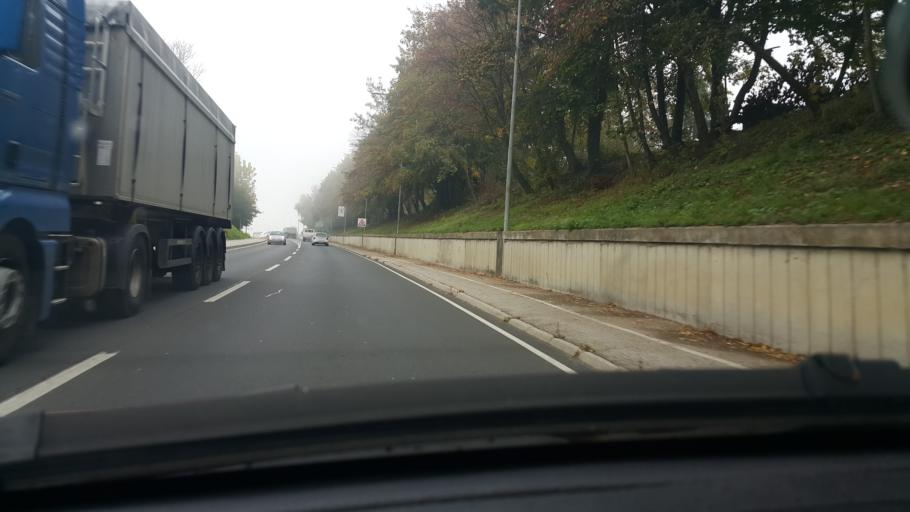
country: SI
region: Brezice
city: Brezice
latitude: 45.9028
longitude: 15.6039
